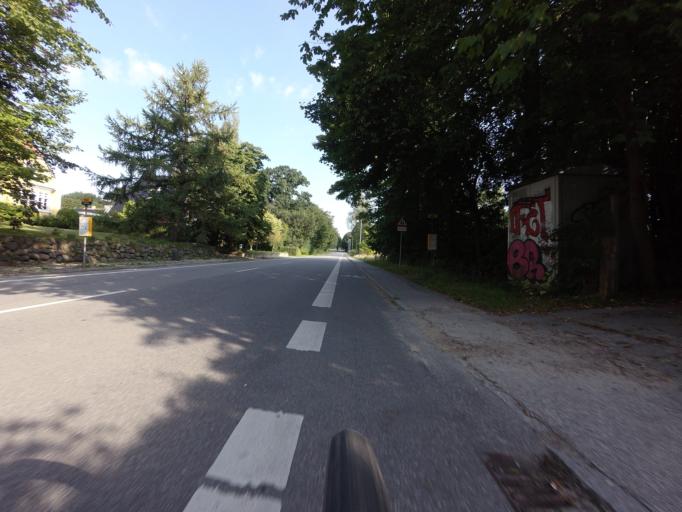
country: DK
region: Zealand
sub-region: Soro Kommune
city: Frederiksberg
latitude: 55.4226
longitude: 11.5671
